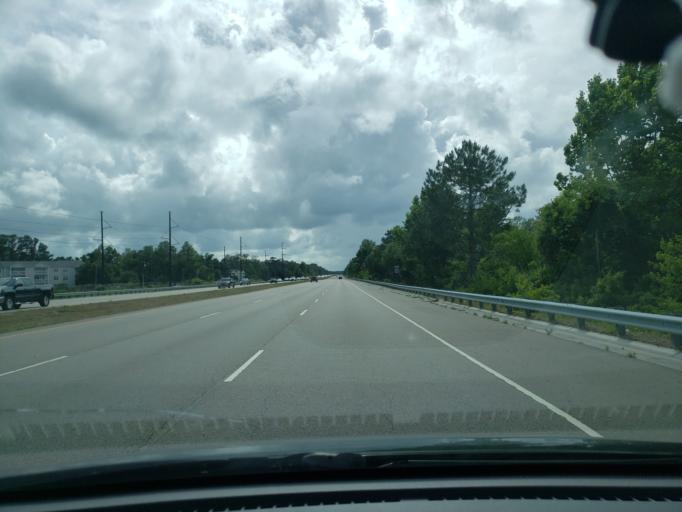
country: US
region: North Carolina
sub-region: New Hanover County
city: Kings Grant
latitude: 34.2552
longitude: -77.8752
